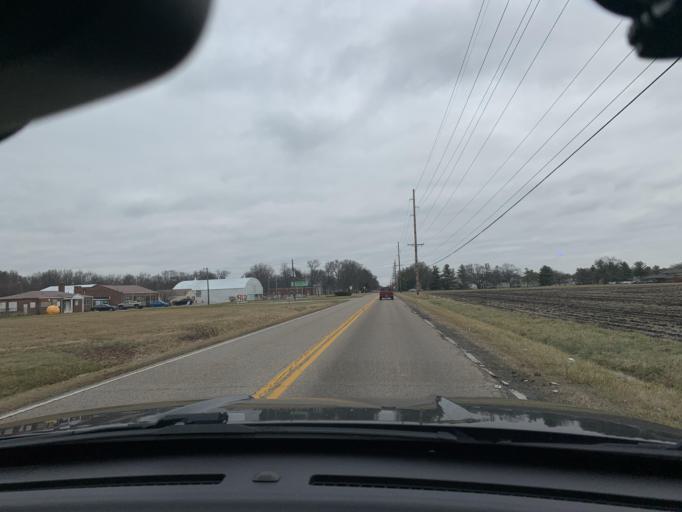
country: US
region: Illinois
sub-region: Sangamon County
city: Jerome
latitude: 39.7538
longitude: -89.6866
